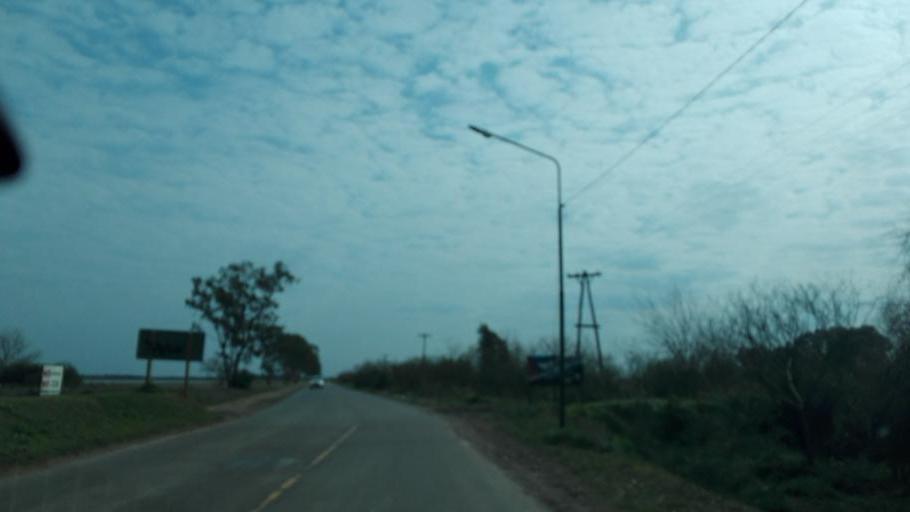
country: AR
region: Buenos Aires
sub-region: Partido de Chascomus
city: Chascomus
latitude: -35.5644
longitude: -58.0315
